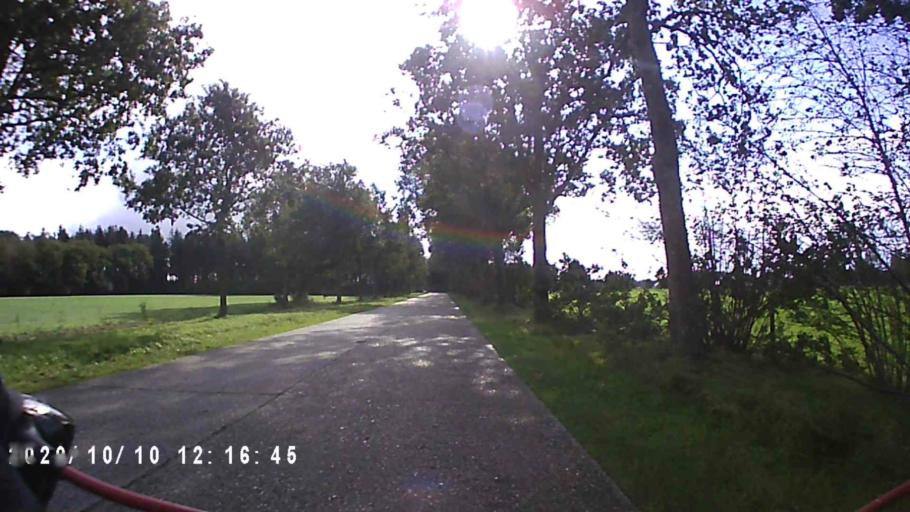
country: NL
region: Friesland
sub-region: Gemeente Heerenveen
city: Jubbega
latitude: 53.0218
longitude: 6.1680
